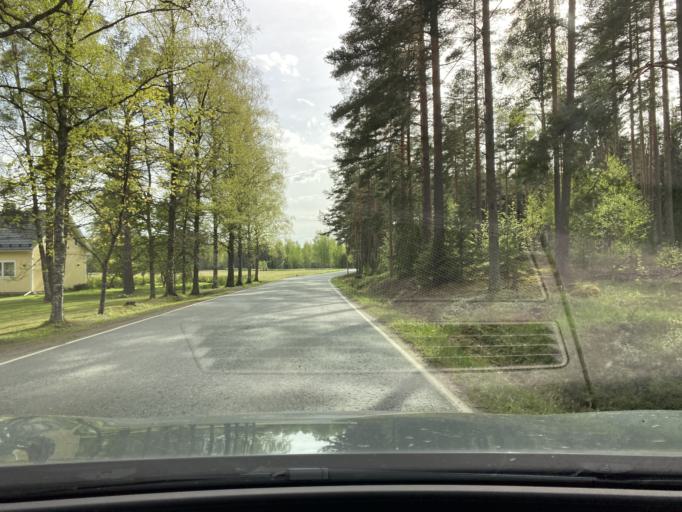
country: FI
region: Varsinais-Suomi
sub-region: Salo
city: Kiikala
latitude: 60.5171
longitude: 23.5359
